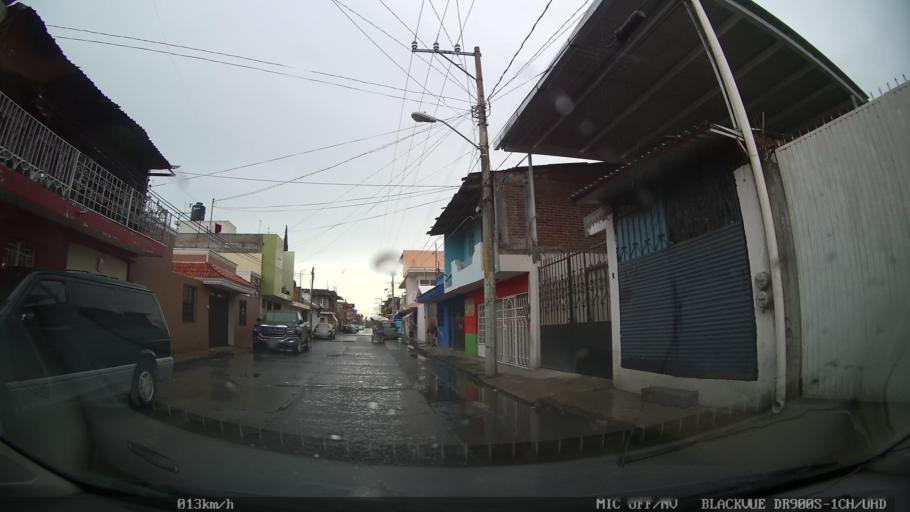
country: MX
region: Michoacan
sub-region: Uruapan
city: Santa Rosa (Santa Barbara)
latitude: 19.4035
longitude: -102.0252
